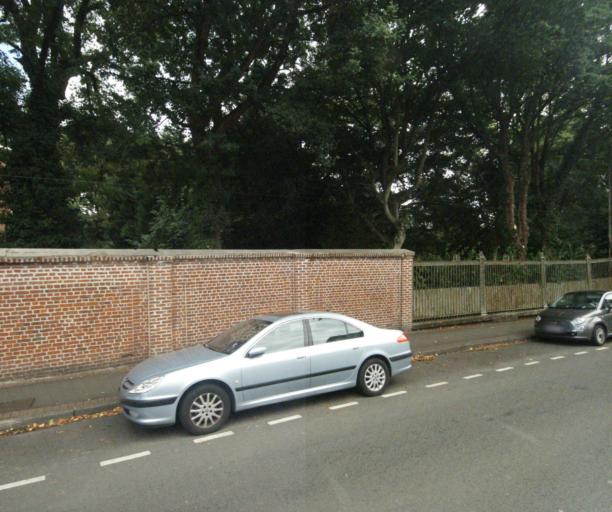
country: FR
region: Nord-Pas-de-Calais
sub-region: Departement du Nord
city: Mons-en-Baroeul
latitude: 50.6444
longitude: 3.1000
